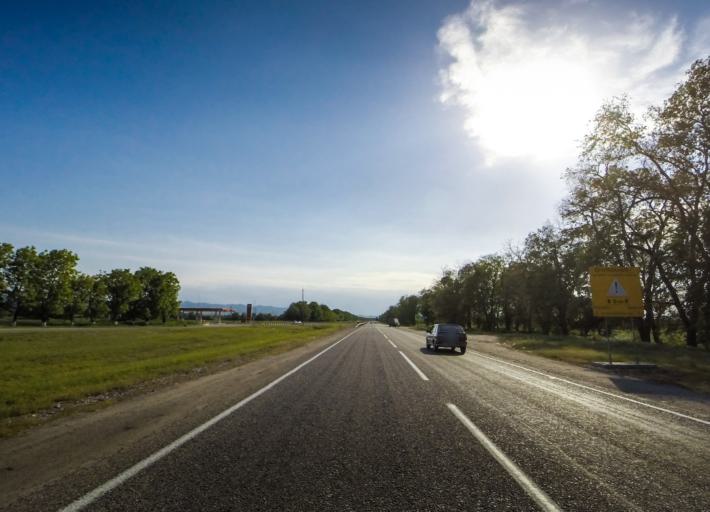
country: RU
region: Kabardino-Balkariya
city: Nartan
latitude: 43.4930
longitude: 43.6927
